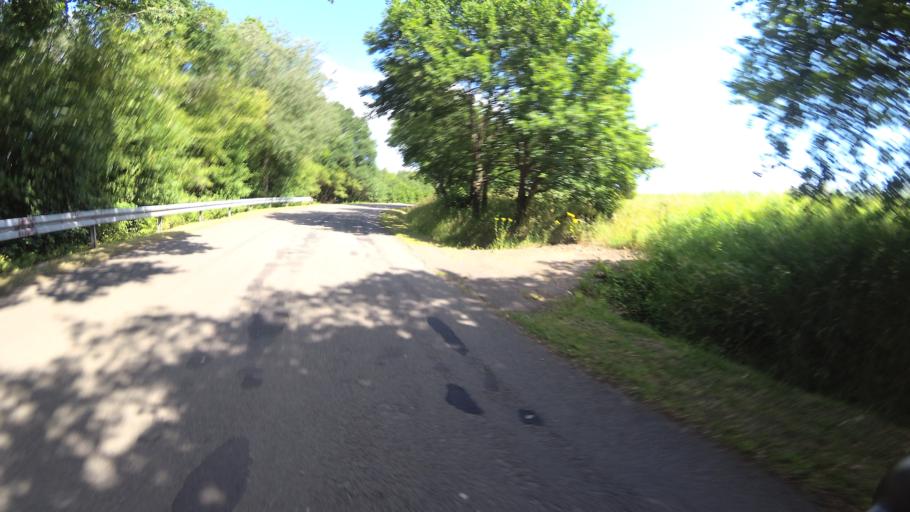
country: DE
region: Saarland
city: Weiskirchen
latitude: 49.5296
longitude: 6.8205
